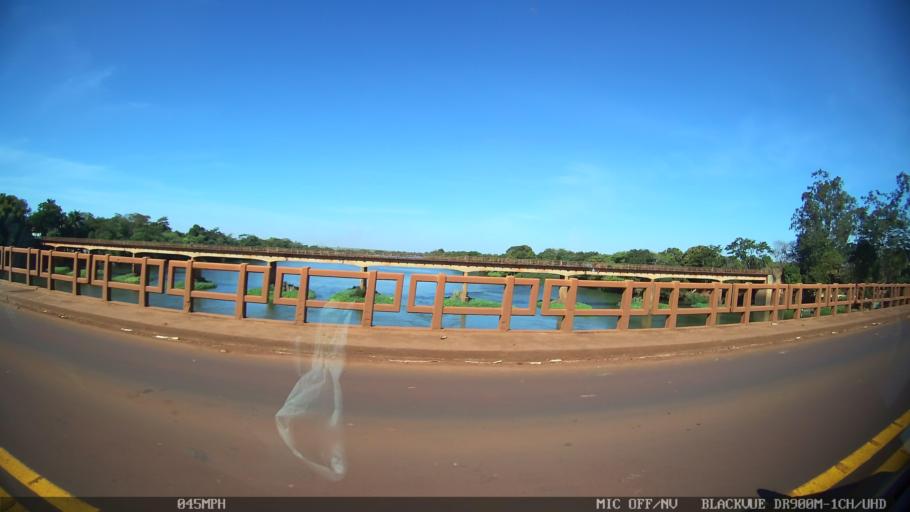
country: BR
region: Sao Paulo
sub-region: Barretos
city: Barretos
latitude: -20.4522
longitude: -48.4562
